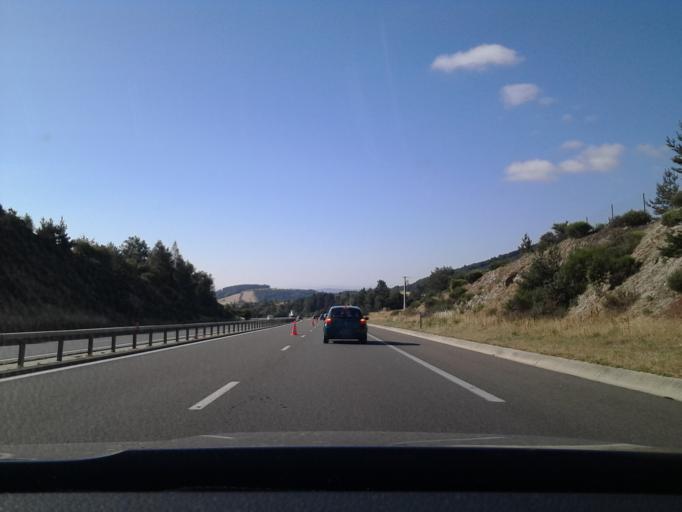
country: FR
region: Languedoc-Roussillon
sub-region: Departement de la Lozere
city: Marvejols
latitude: 44.6282
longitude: 3.2441
